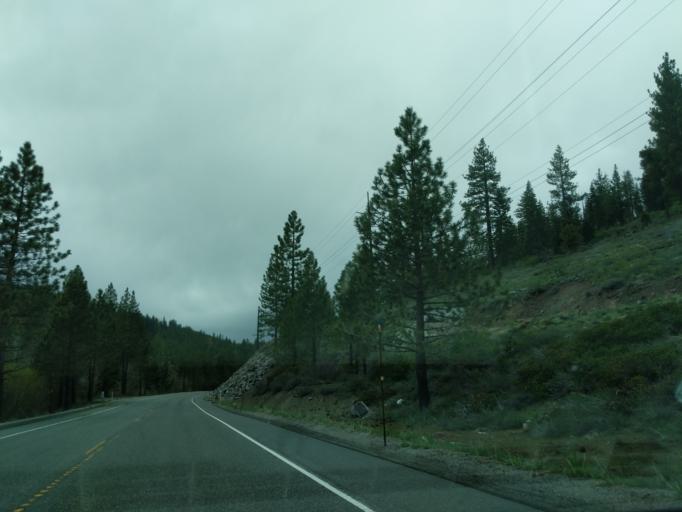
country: US
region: California
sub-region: Placer County
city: Tahoe Vista
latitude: 39.2707
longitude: -120.0901
